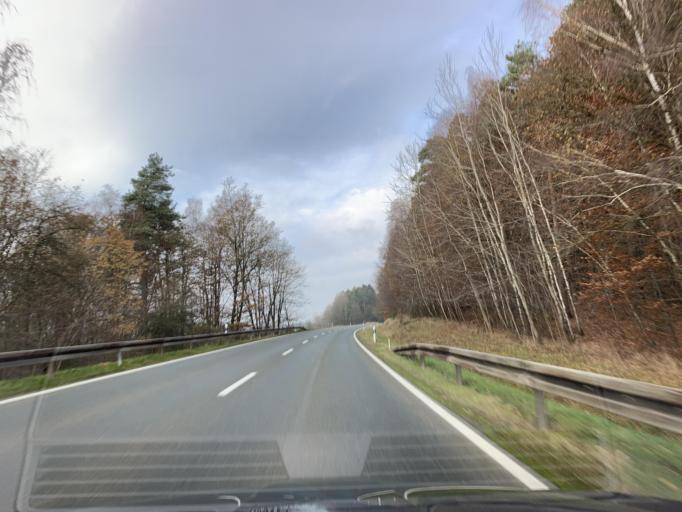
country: DE
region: Bavaria
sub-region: Upper Palatinate
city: Thanstein
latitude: 49.3467
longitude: 12.4691
